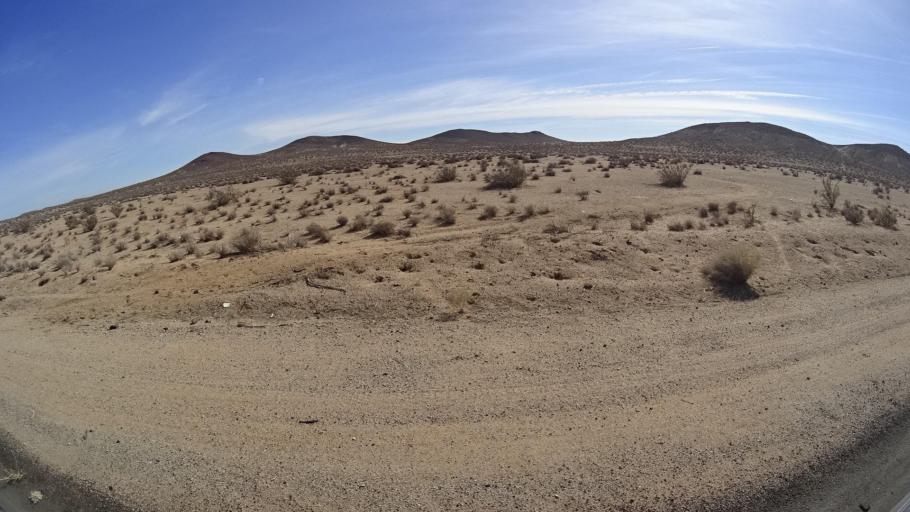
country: US
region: California
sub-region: Kern County
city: North Edwards
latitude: 35.0453
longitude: -117.8213
